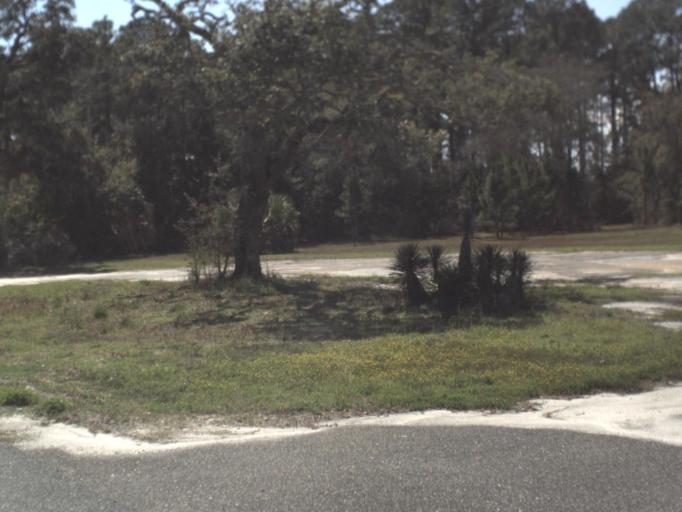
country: US
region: Florida
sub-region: Wakulla County
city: Crawfordville
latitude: 30.0255
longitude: -84.3903
